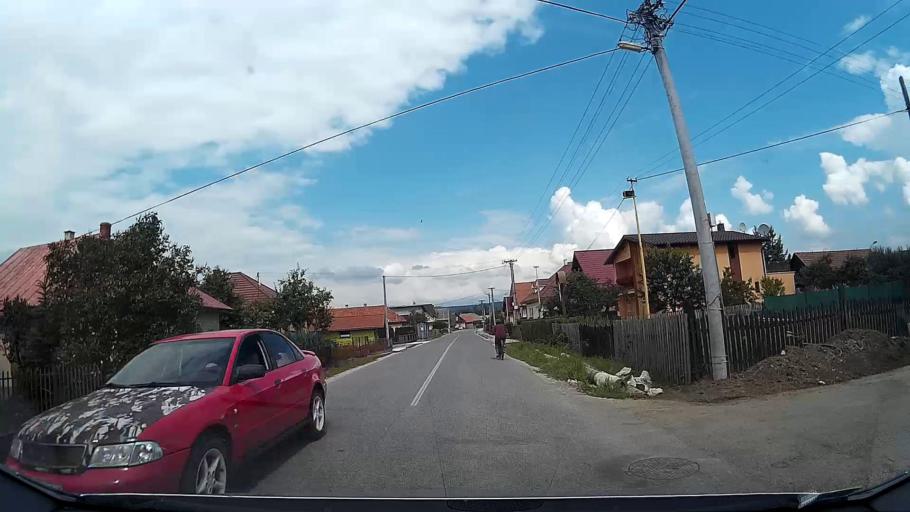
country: SK
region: Presovsky
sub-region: Okres Poprad
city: Poprad
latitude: 48.9757
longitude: 20.3934
